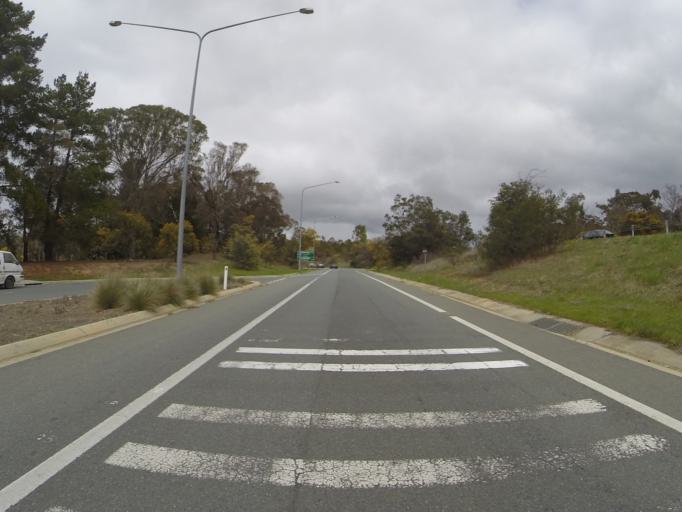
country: AU
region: Australian Capital Territory
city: Kaleen
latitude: -35.2116
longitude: 149.1899
